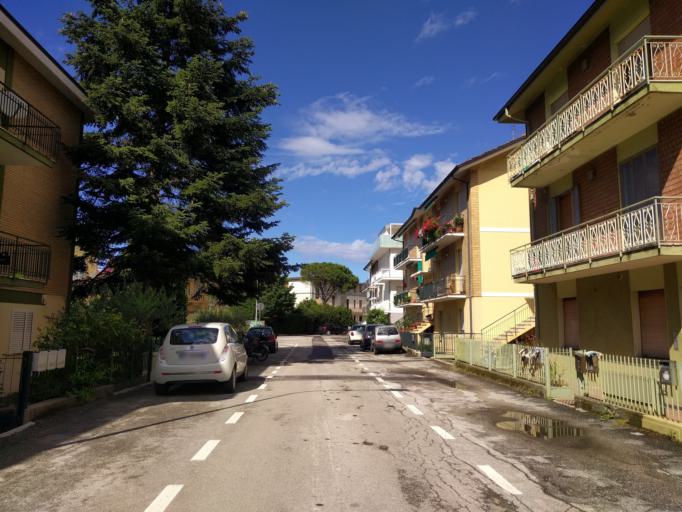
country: IT
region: The Marches
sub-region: Provincia di Pesaro e Urbino
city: Pesaro
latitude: 43.8952
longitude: 12.9119
